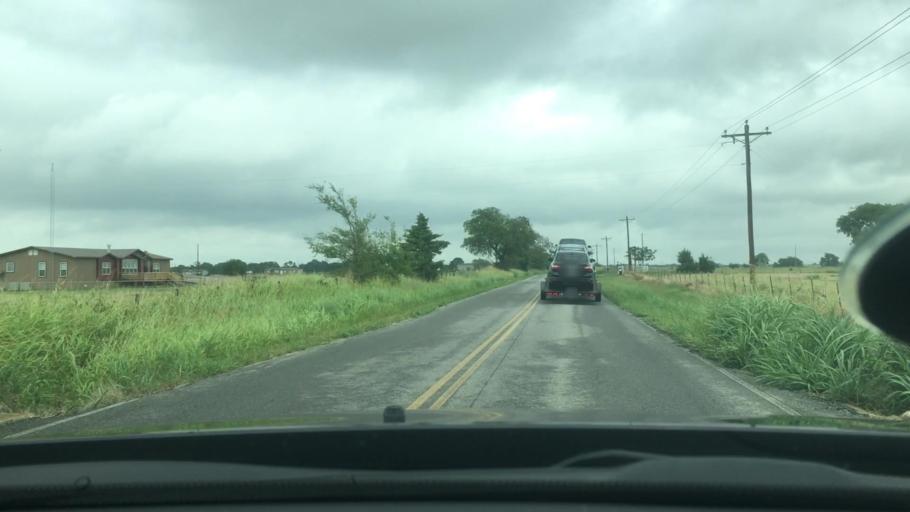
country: US
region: Oklahoma
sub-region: Bryan County
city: Colbert
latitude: 33.9182
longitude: -96.5006
